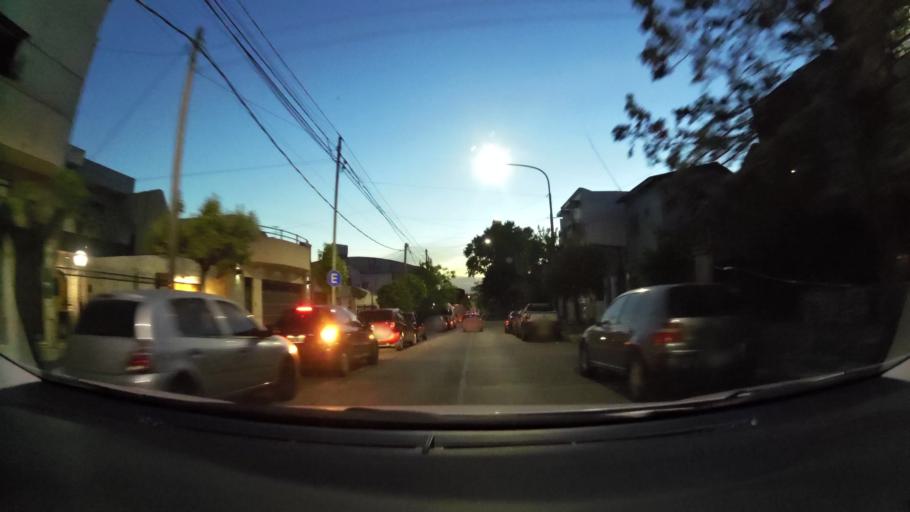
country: AR
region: Buenos Aires F.D.
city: Villa Lugano
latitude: -34.6845
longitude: -58.4785
